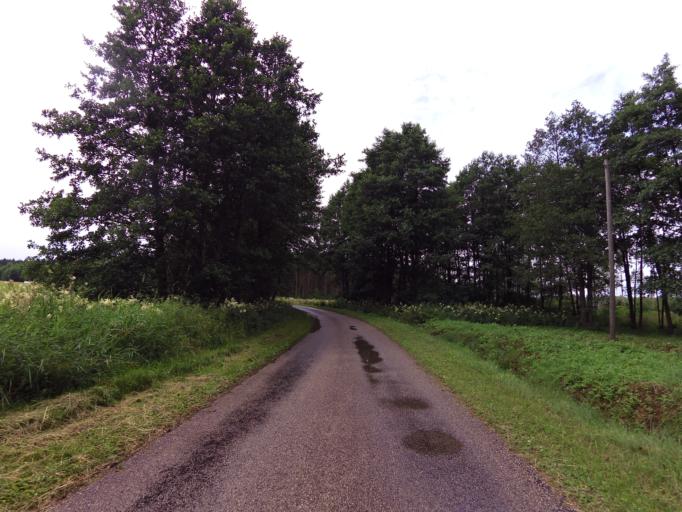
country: EE
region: Laeaene
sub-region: Vormsi vald
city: Hullo
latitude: 59.0038
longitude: 23.3469
